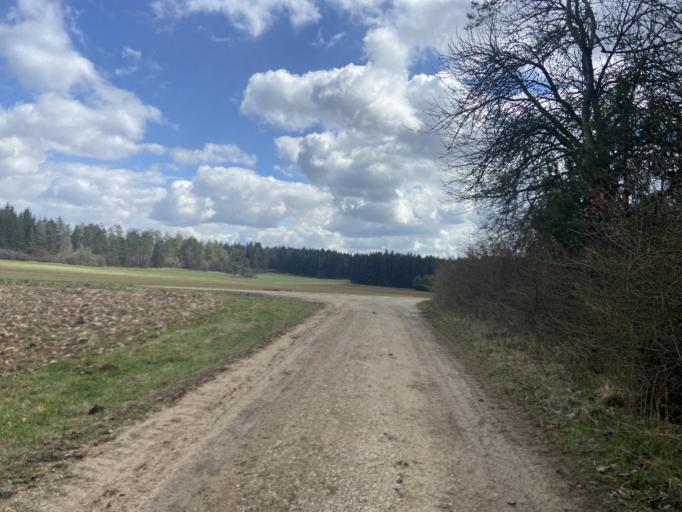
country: DE
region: Baden-Wuerttemberg
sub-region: Tuebingen Region
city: Veringenstadt
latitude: 48.1447
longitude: 9.2372
